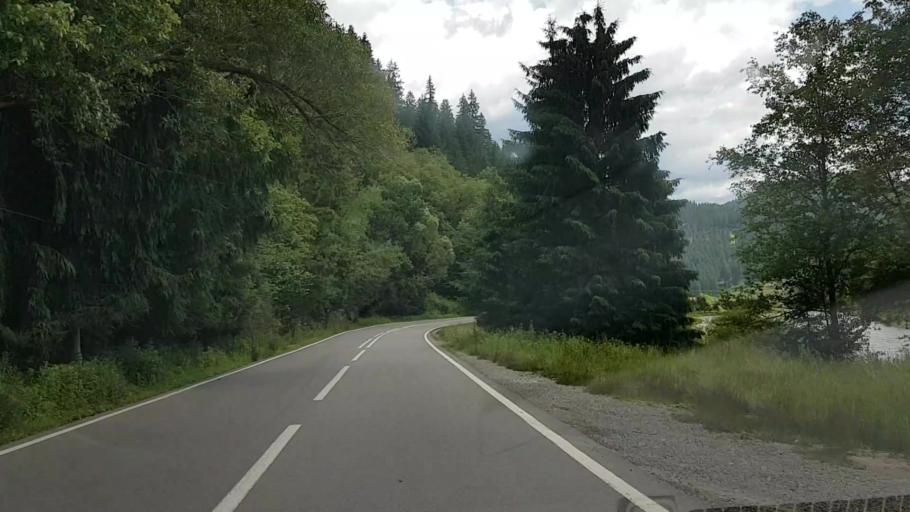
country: RO
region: Suceava
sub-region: Comuna Crucea
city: Crucea
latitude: 47.3626
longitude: 25.6023
